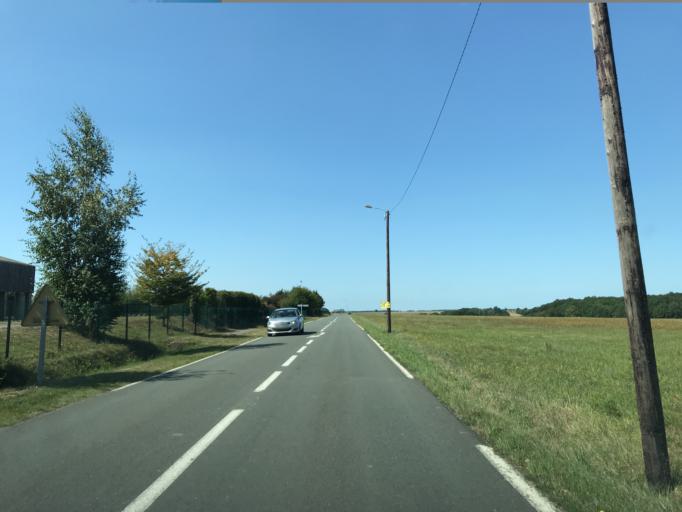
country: FR
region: Haute-Normandie
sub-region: Departement de l'Eure
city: La Chapelle-Reanville
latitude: 49.0960
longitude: 1.3883
